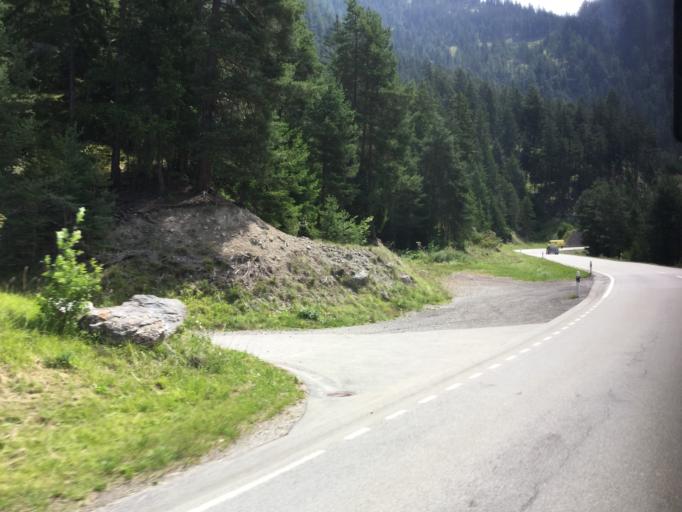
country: CH
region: Grisons
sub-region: Albula District
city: Tiefencastel
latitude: 46.6453
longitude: 9.5836
